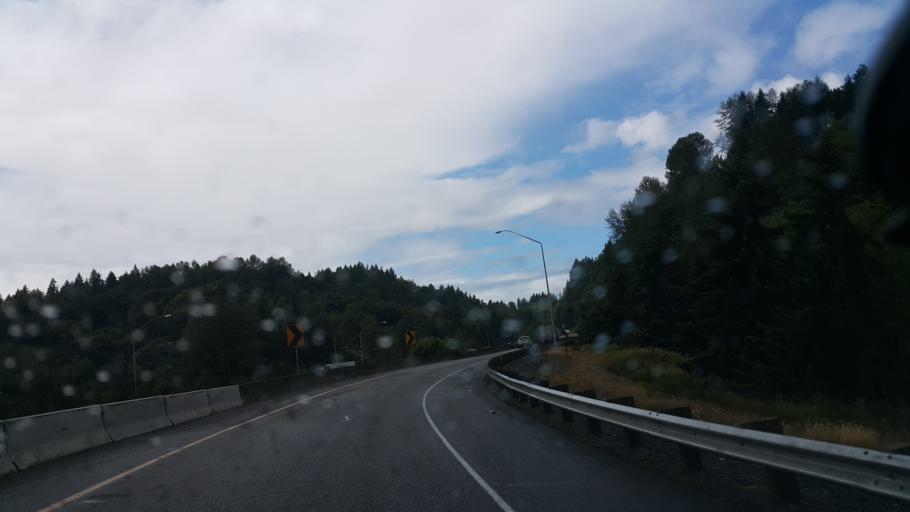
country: US
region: Washington
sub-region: King County
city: Algona
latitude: 47.3038
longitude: -122.2539
